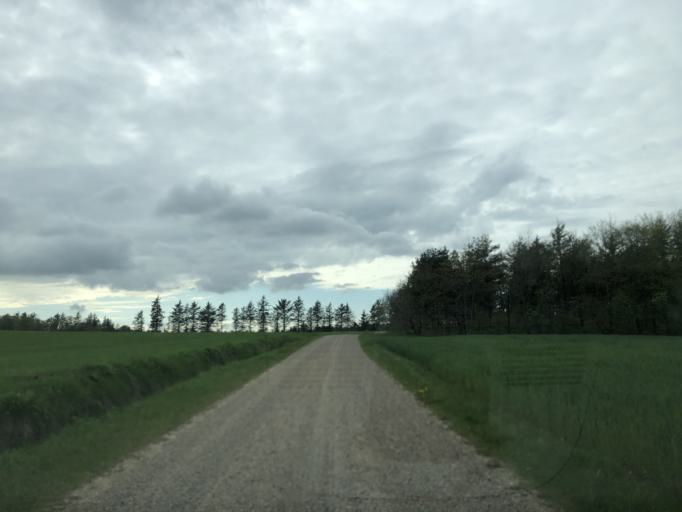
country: DK
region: Central Jutland
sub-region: Holstebro Kommune
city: Ulfborg
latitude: 56.1978
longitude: 8.4406
